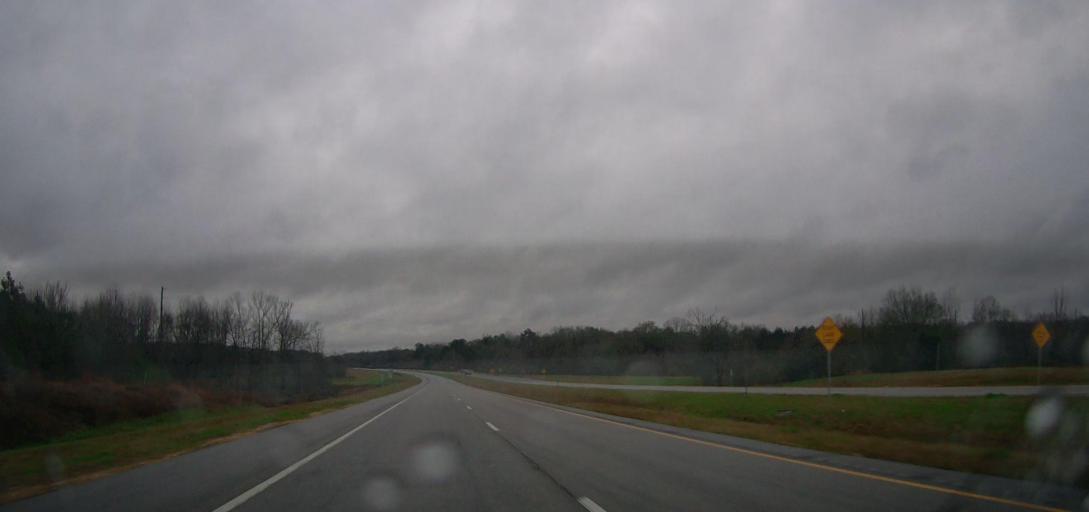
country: US
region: Alabama
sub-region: Bibb County
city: Centreville
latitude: 32.9367
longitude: -87.0640
